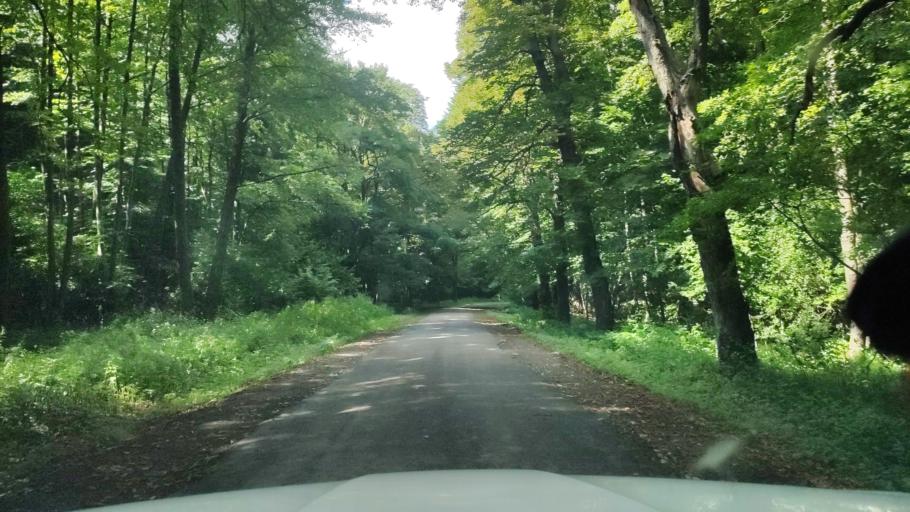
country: HU
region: Heves
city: Parad
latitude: 47.8999
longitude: 20.0563
